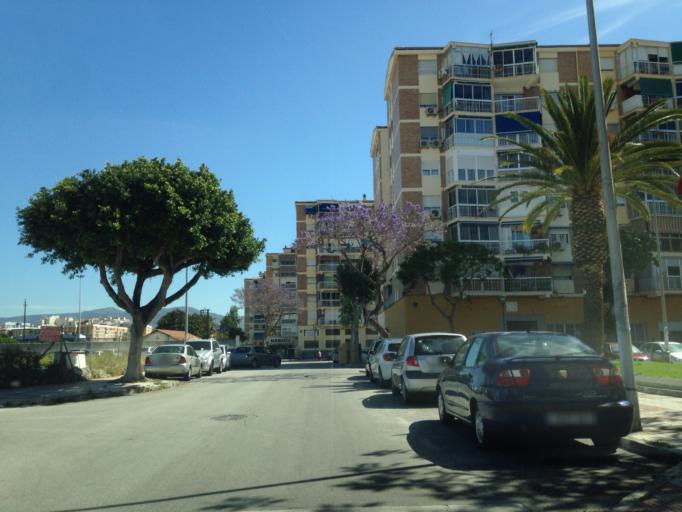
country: ES
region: Andalusia
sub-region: Provincia de Malaga
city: Malaga
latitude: 36.7062
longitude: -4.4396
